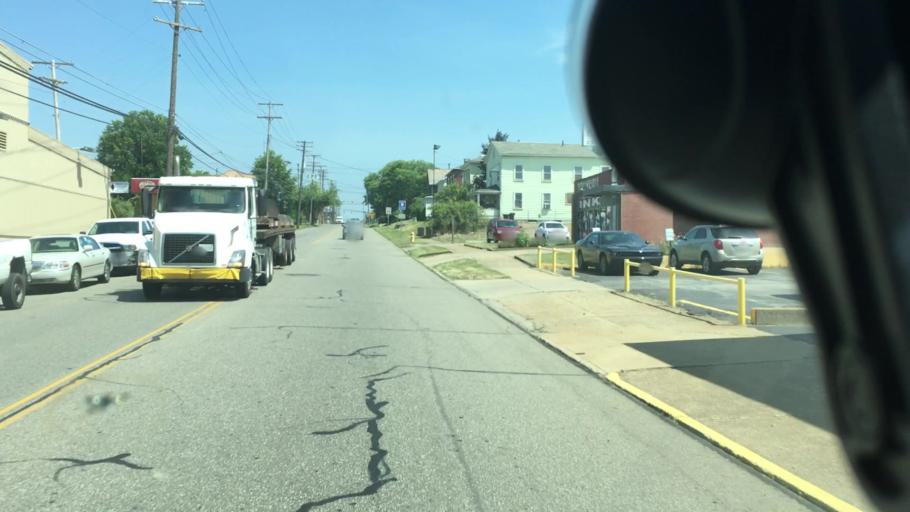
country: US
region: Ohio
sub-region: Columbiana County
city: Salem
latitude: 40.8966
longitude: -80.8567
